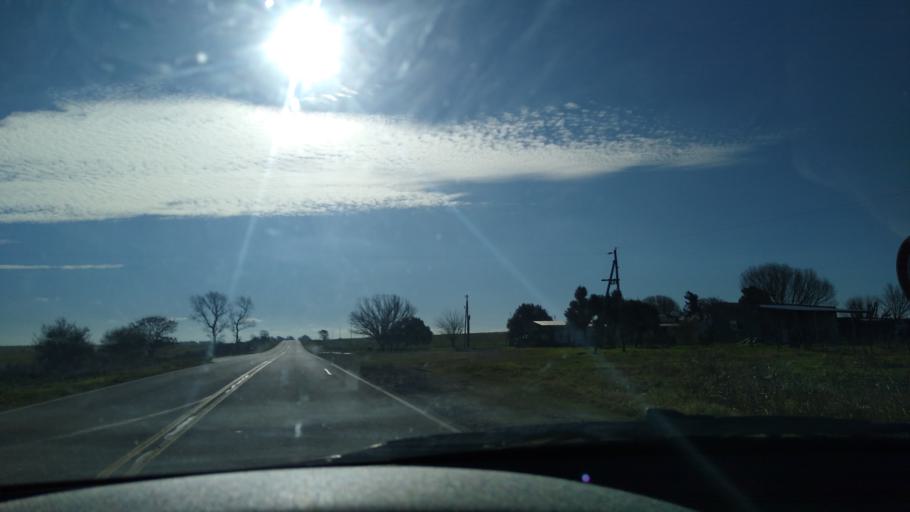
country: AR
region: Entre Rios
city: Aranguren
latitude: -32.3489
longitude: -60.3648
